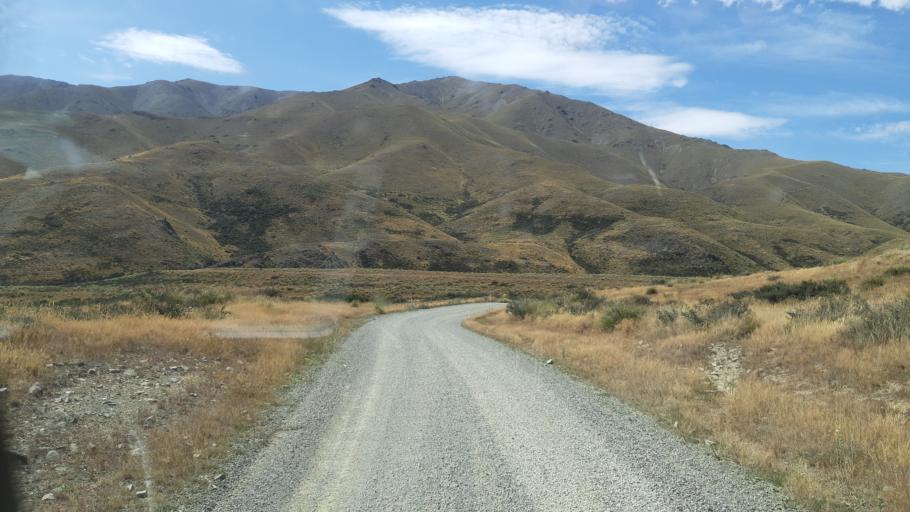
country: NZ
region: Canterbury
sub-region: Timaru District
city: Pleasant Point
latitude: -44.2930
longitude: 170.5608
